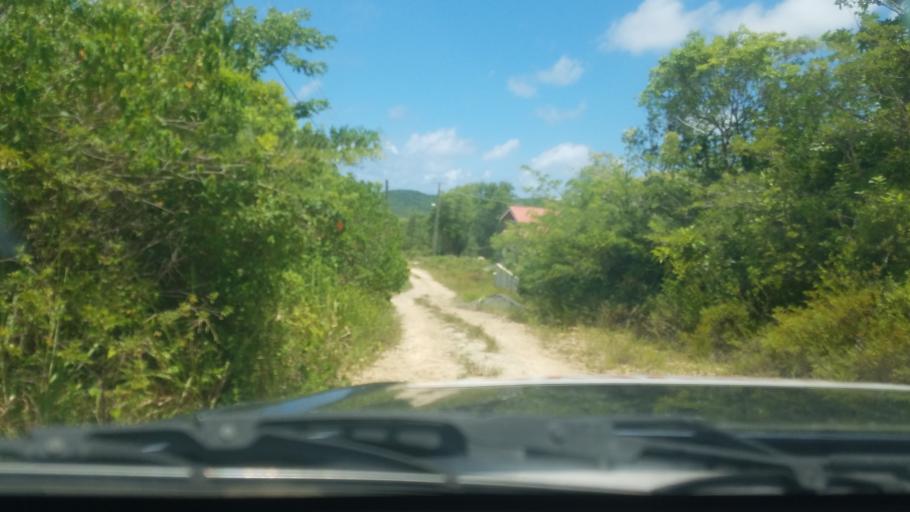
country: LC
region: Dennery Quarter
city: Dennery
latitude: 13.9208
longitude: -60.9015
